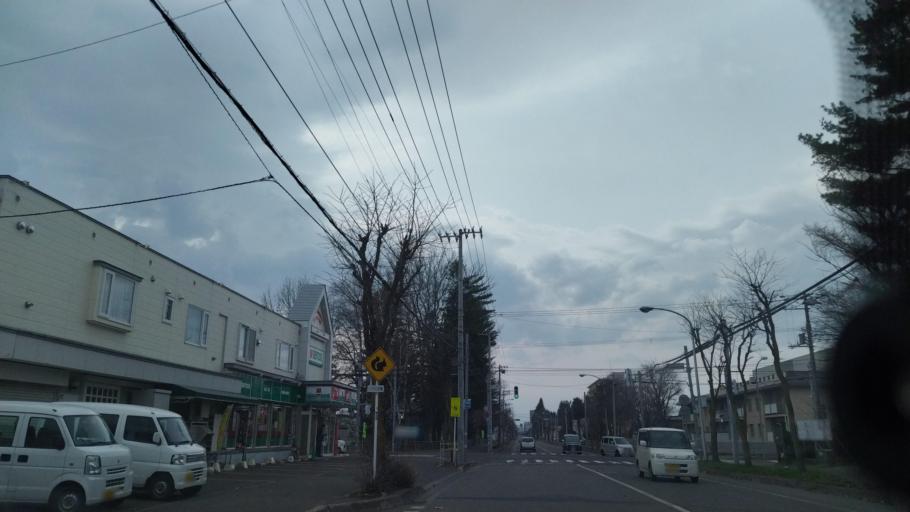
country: JP
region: Hokkaido
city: Obihiro
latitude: 42.9225
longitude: 143.2196
